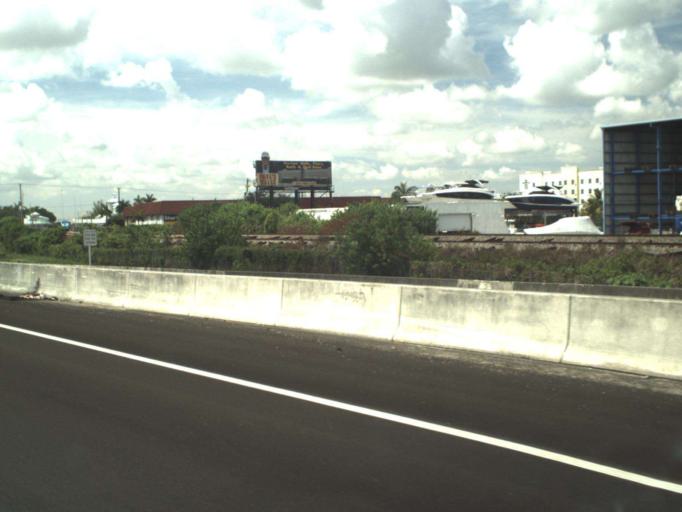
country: US
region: Florida
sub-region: Broward County
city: Dania Beach
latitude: 26.0661
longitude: -80.1652
